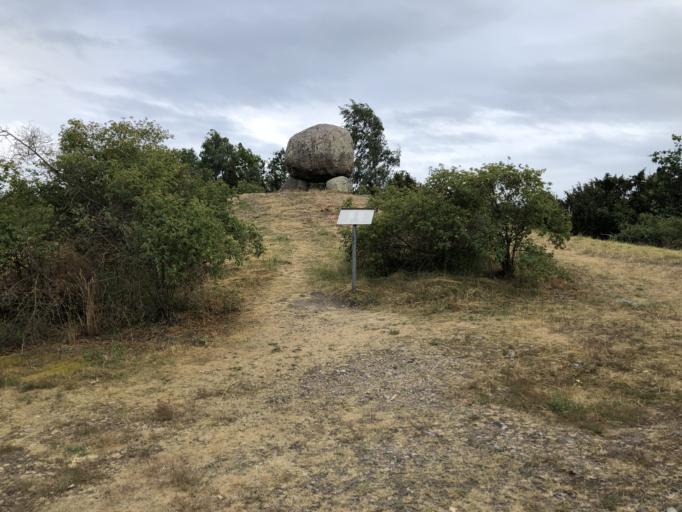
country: SE
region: Kalmar
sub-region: Kalmar Kommun
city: Kalmar
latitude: 56.6325
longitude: 16.3181
